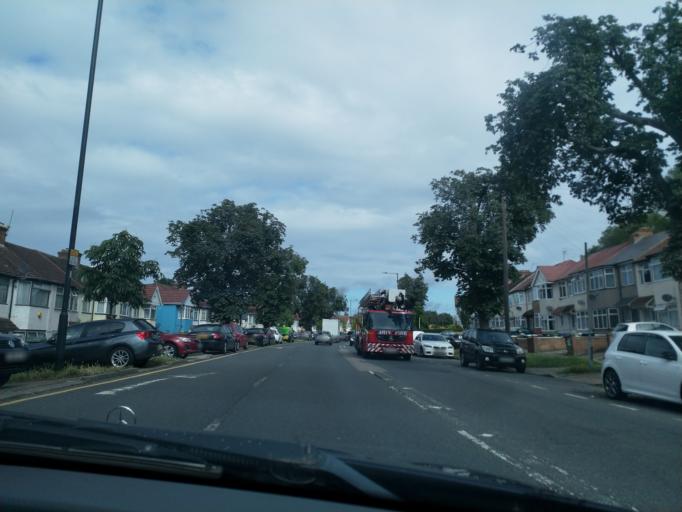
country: GB
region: England
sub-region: Greater London
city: Wembley
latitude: 51.5415
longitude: -0.3034
